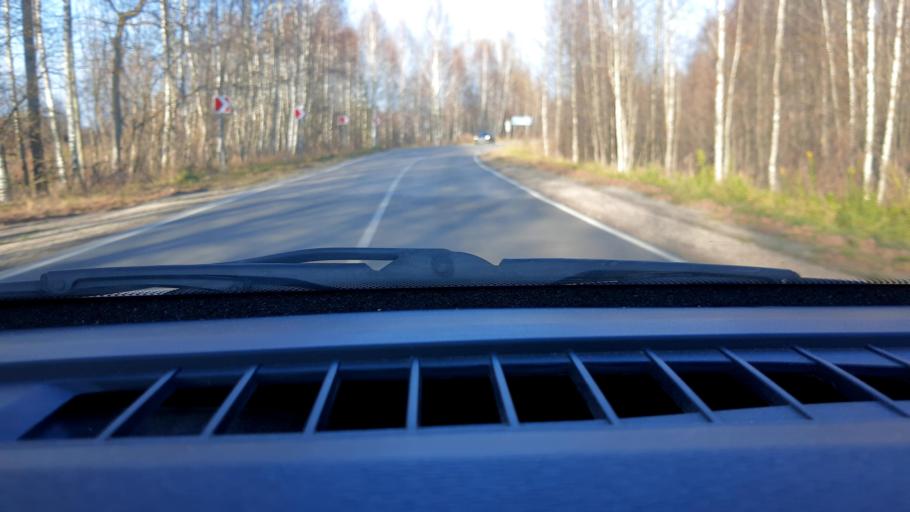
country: RU
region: Nizjnij Novgorod
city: Neklyudovo
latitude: 56.4997
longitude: 43.8517
